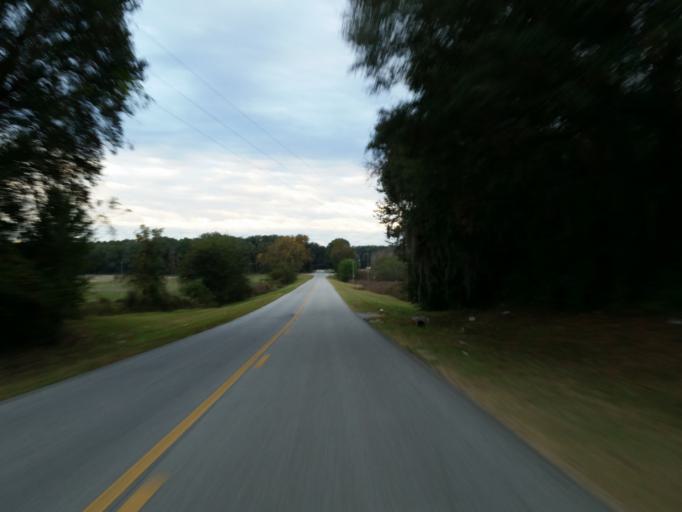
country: US
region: Florida
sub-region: Hamilton County
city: Jasper
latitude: 30.5311
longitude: -83.1026
